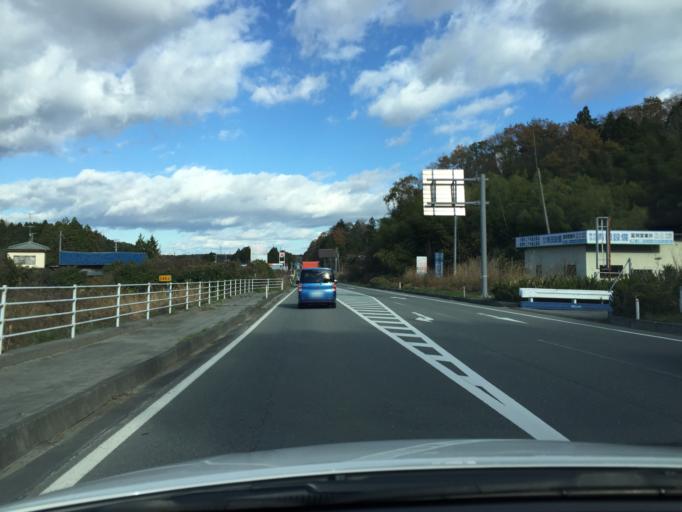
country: JP
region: Fukushima
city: Namie
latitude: 37.3720
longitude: 141.0091
